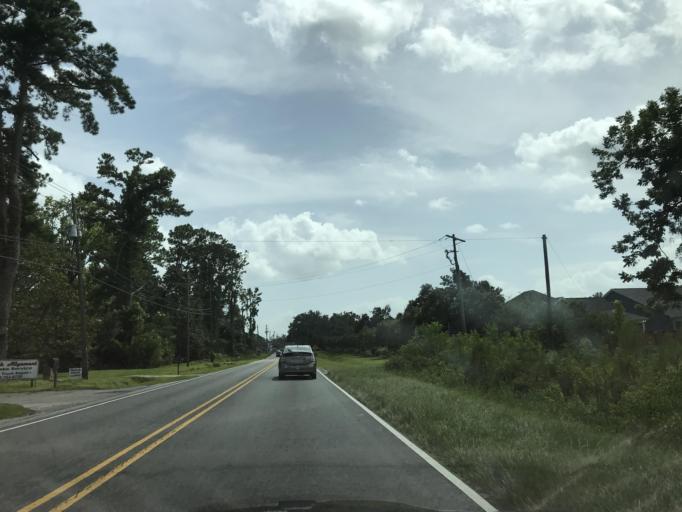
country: US
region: North Carolina
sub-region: New Hanover County
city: Wrightsboro
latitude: 34.2790
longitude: -77.9241
